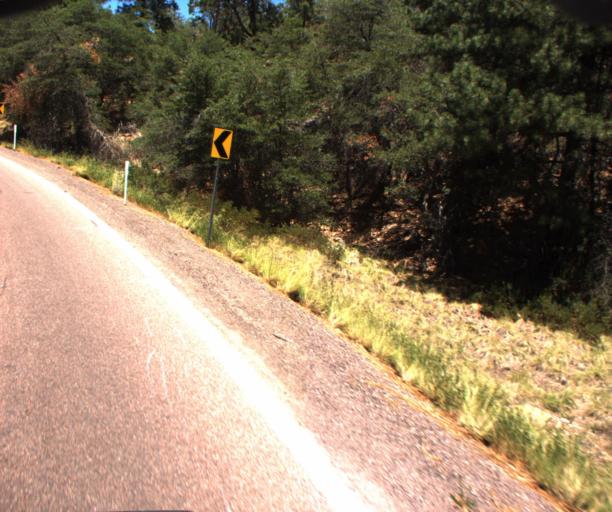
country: US
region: Arizona
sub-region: Gila County
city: Pine
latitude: 34.4215
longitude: -111.5086
